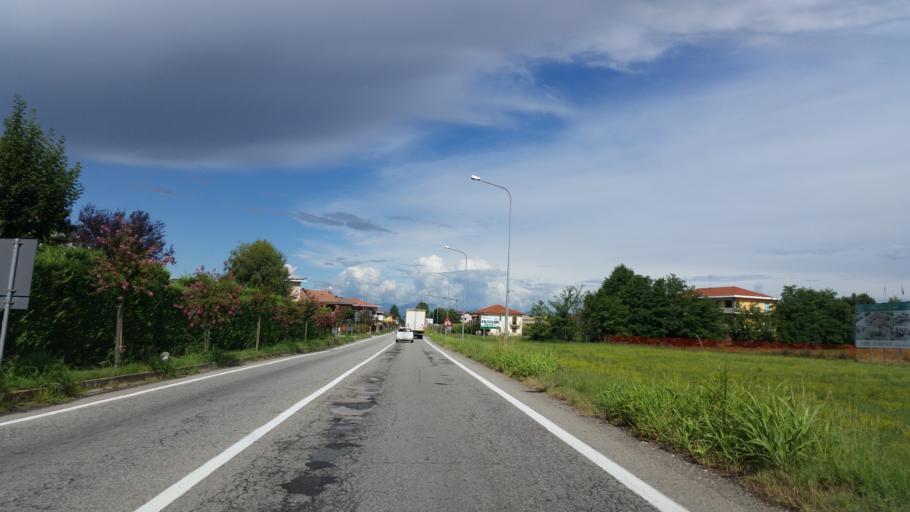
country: IT
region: Piedmont
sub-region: Provincia di Torino
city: Marocchi
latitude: 44.9410
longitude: 7.8190
